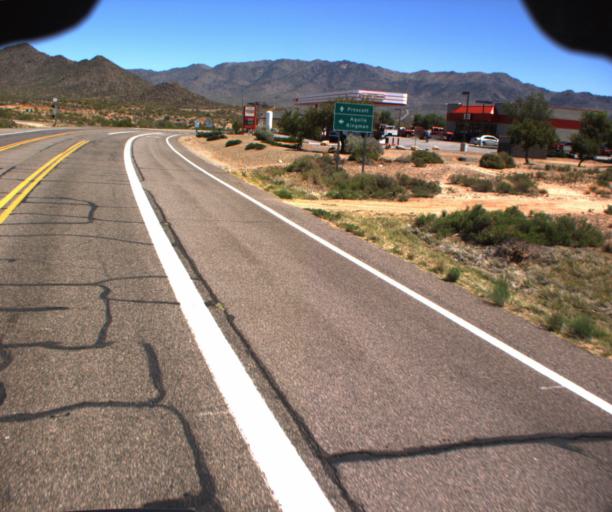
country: US
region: Arizona
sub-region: Yavapai County
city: Congress
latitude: 34.1616
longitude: -112.8447
